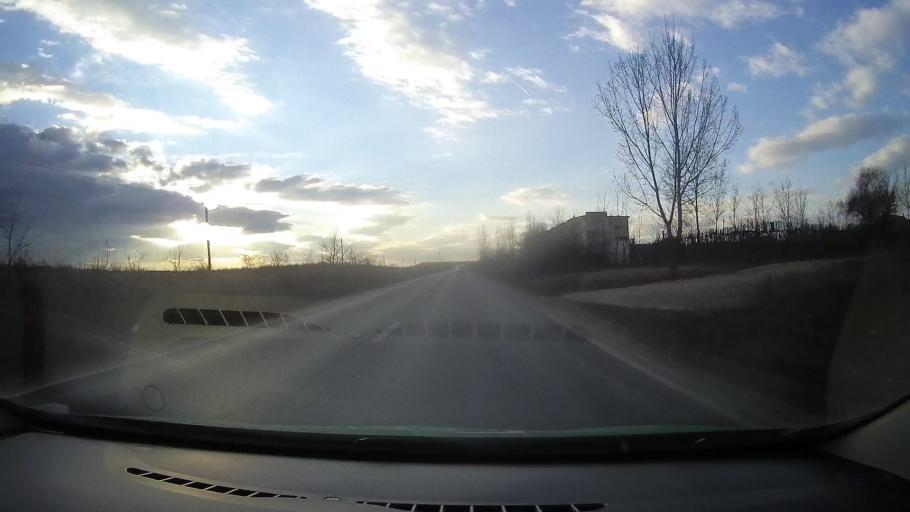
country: RO
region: Dambovita
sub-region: Comuna I. L. Caragiale
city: Mija
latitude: 44.9121
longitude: 25.6793
